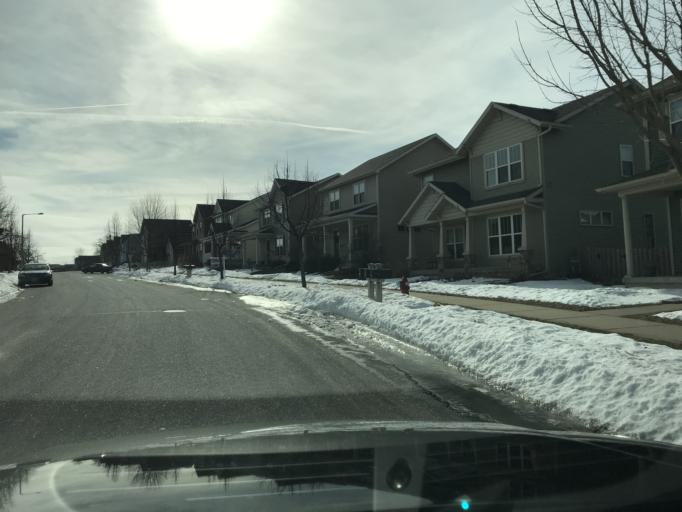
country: US
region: Wisconsin
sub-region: Dane County
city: Monona
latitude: 43.0891
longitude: -89.2800
